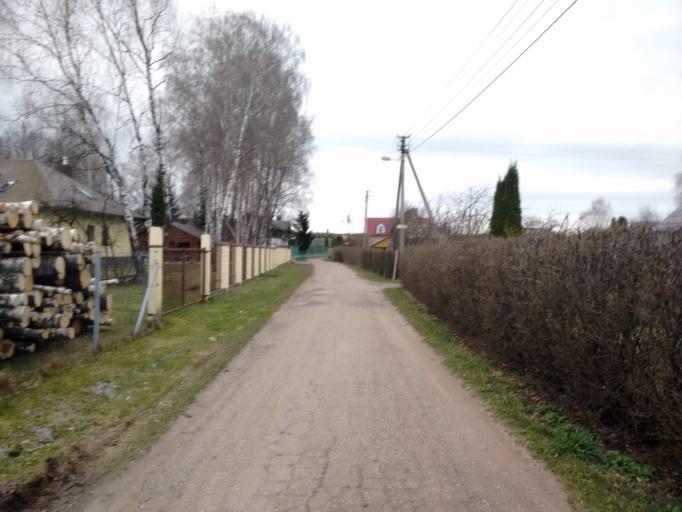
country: LT
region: Vilnius County
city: Rasos
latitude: 54.7915
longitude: 25.3615
